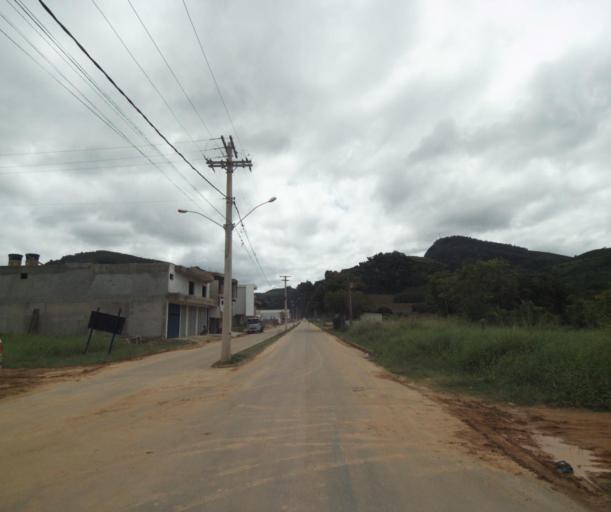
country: BR
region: Espirito Santo
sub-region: Irupi
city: Irupi
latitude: -20.3408
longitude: -41.6436
